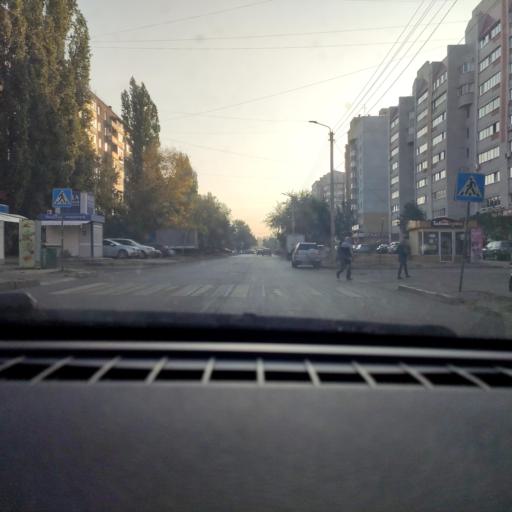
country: RU
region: Voronezj
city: Maslovka
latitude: 51.5949
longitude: 39.2412
